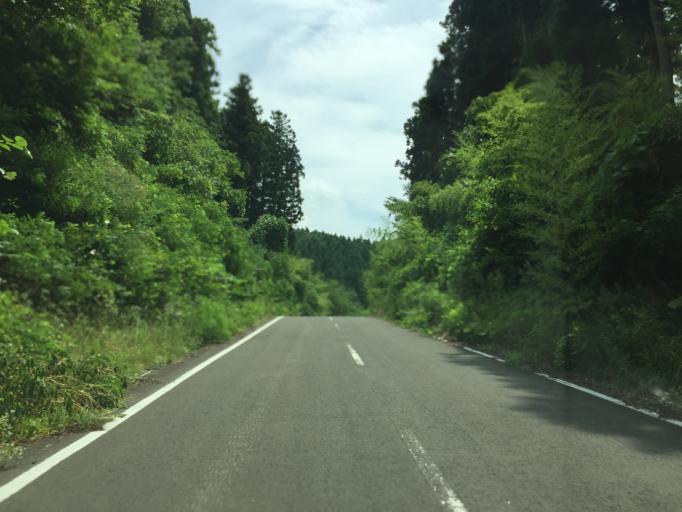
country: JP
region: Fukushima
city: Hobaramachi
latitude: 37.6449
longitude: 140.6559
